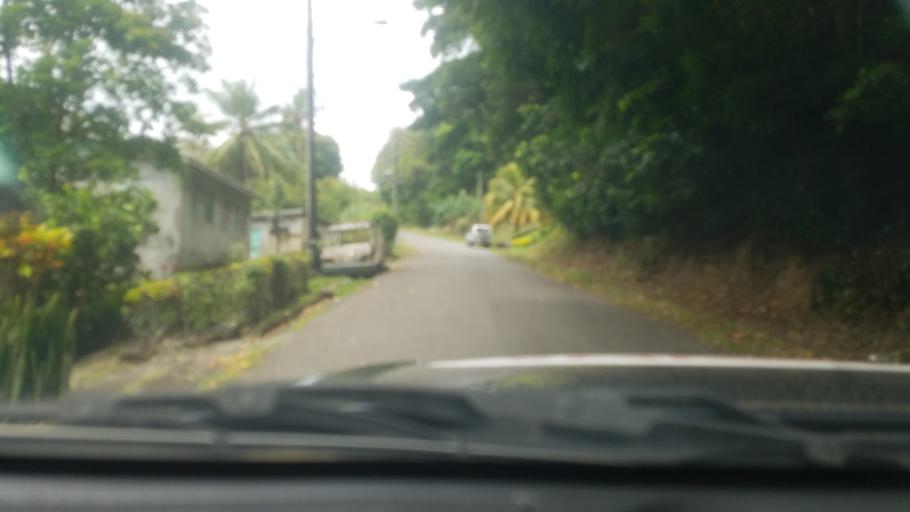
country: LC
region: Laborie Quarter
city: Laborie
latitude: 13.7952
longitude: -60.9523
